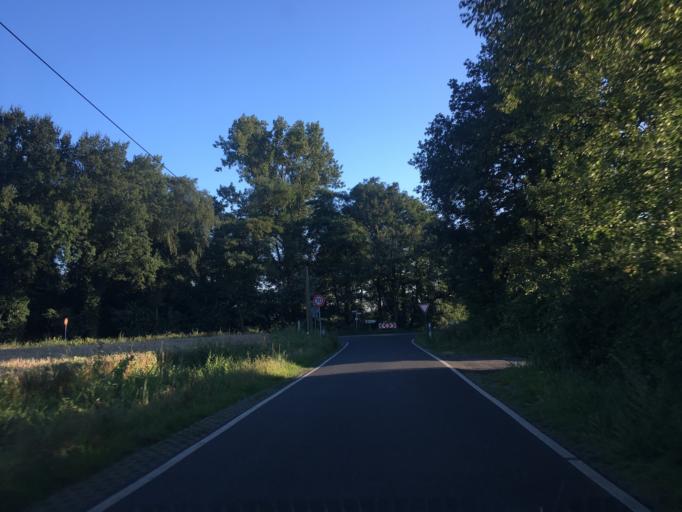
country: DE
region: North Rhine-Westphalia
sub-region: Regierungsbezirk Munster
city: Muenster
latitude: 51.9069
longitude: 7.6094
